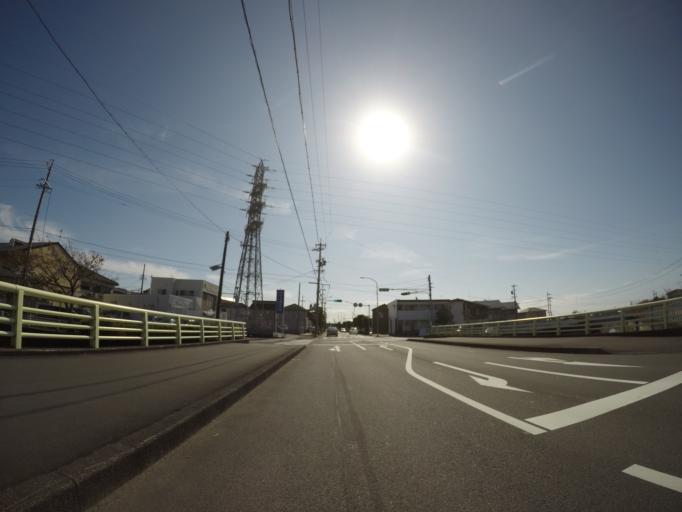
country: JP
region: Shizuoka
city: Shizuoka-shi
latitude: 34.9682
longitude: 138.4217
